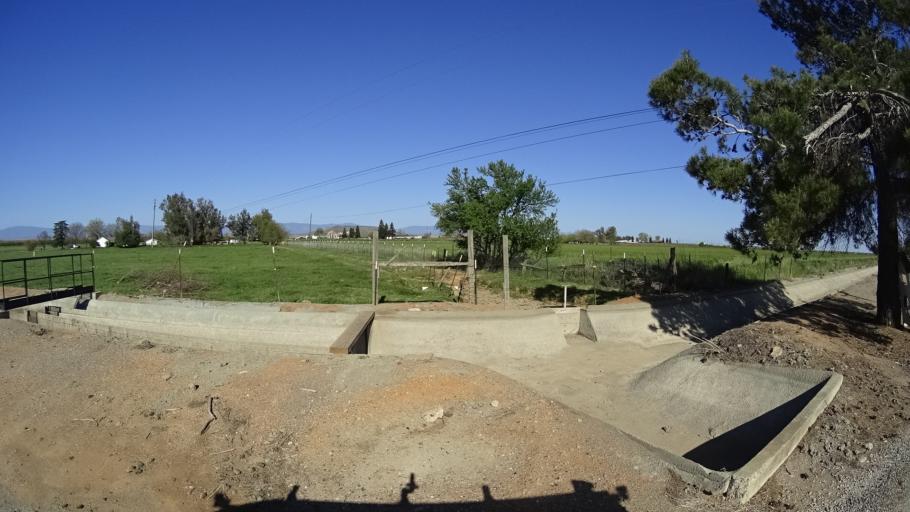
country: US
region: California
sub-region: Glenn County
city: Orland
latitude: 39.7333
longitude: -122.2482
